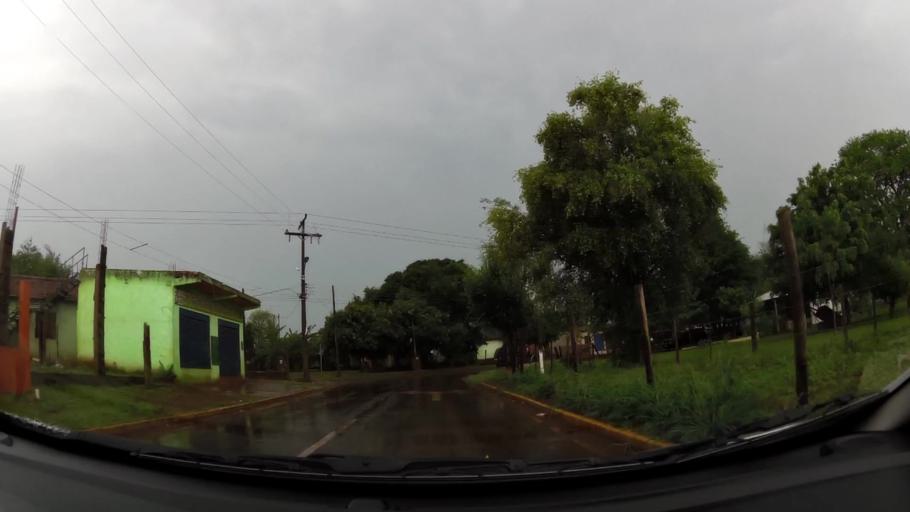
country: PY
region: Alto Parana
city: Presidente Franco
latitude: -25.5513
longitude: -54.6612
